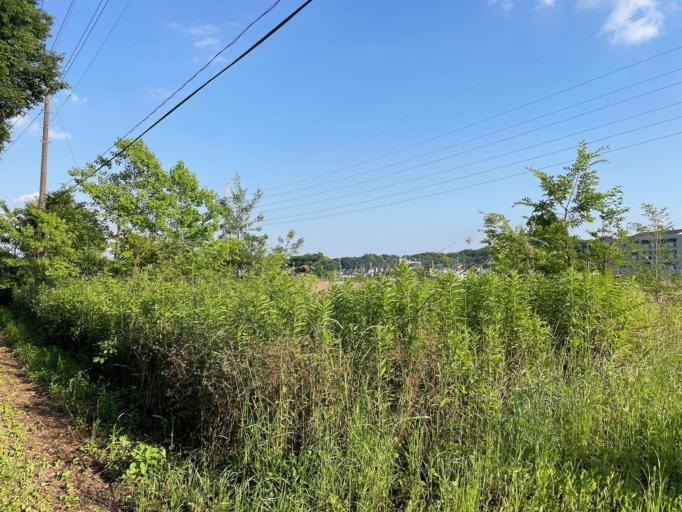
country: JP
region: Saitama
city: Sakado
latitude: 36.0039
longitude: 139.3765
